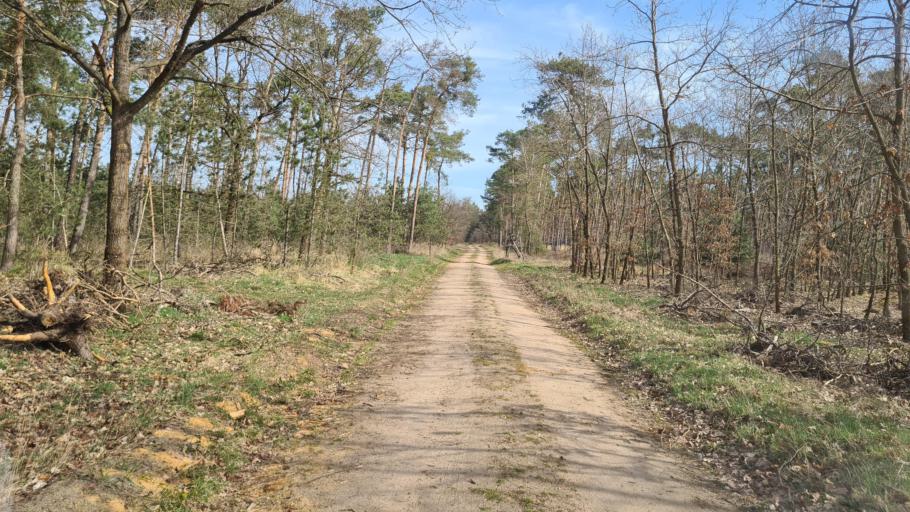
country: DE
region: Saxony
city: Nauwalde
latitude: 51.4614
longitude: 13.3960
